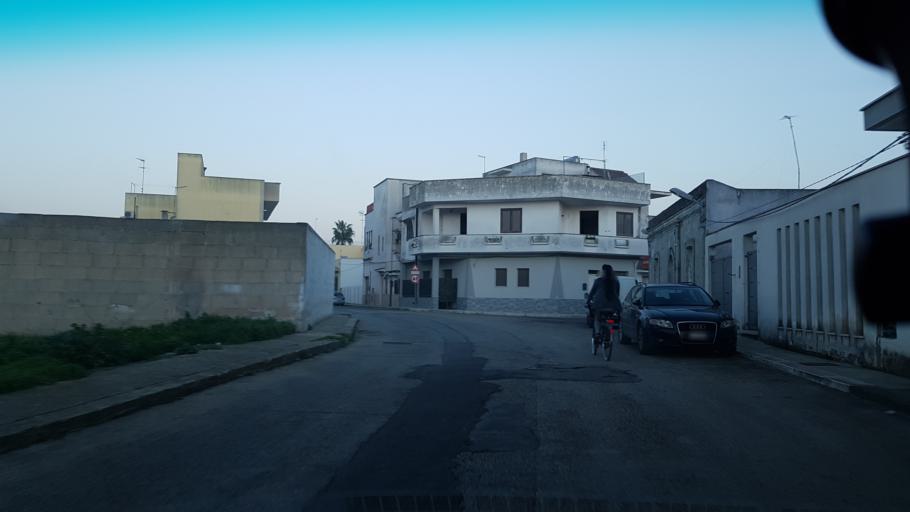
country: IT
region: Apulia
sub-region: Provincia di Brindisi
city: Mesagne
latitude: 40.5633
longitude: 17.7973
